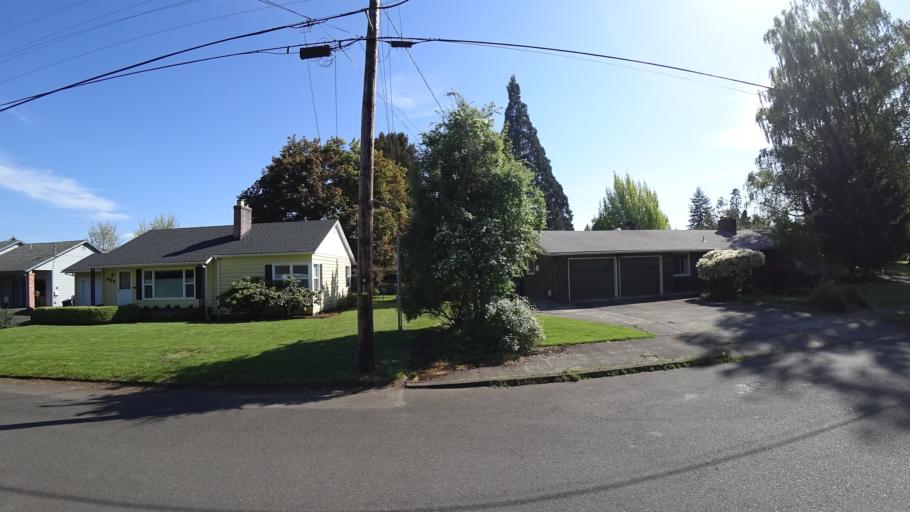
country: US
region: Oregon
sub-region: Washington County
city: Hillsboro
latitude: 45.5262
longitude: -122.9793
